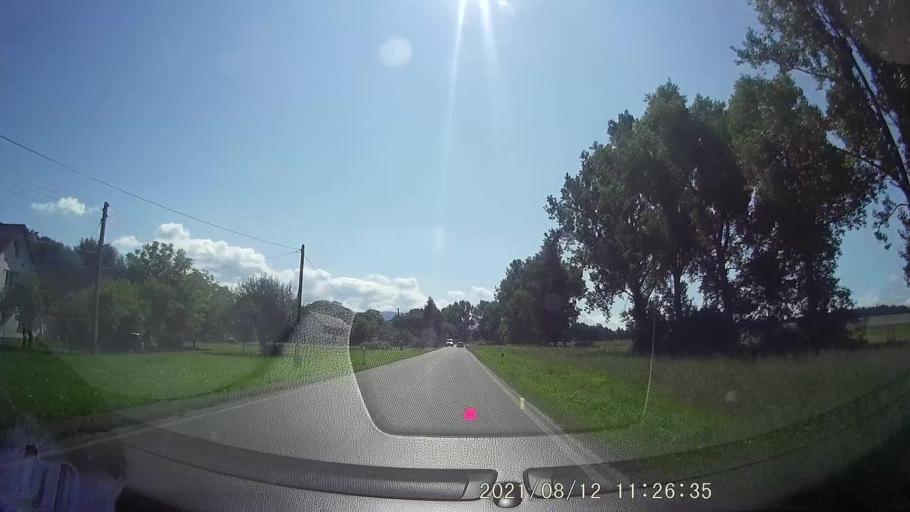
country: PL
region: Lower Silesian Voivodeship
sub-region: Powiat klodzki
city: Bystrzyca Klodzka
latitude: 50.2758
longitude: 16.6863
